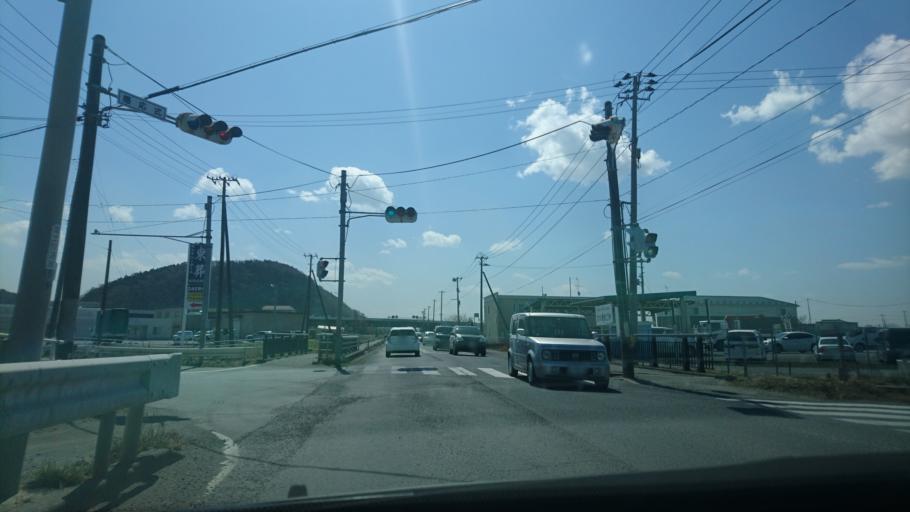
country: JP
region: Miyagi
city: Ishinomaki
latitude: 38.4690
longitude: 141.2844
